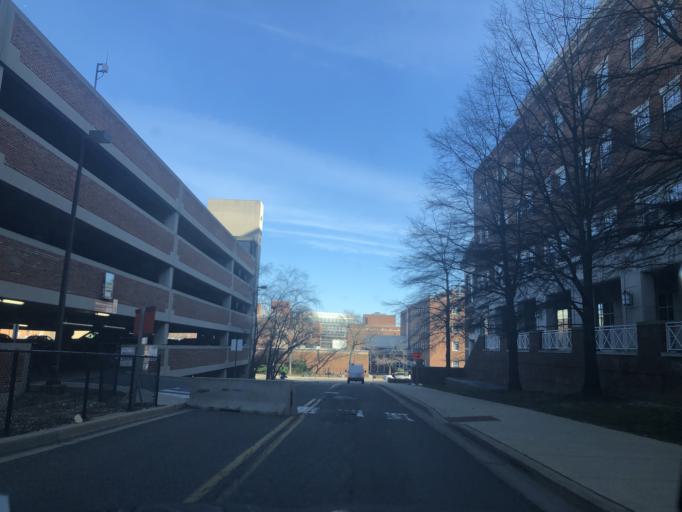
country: US
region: Maryland
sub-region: Prince George's County
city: College Park
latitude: 38.9890
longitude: -76.9418
